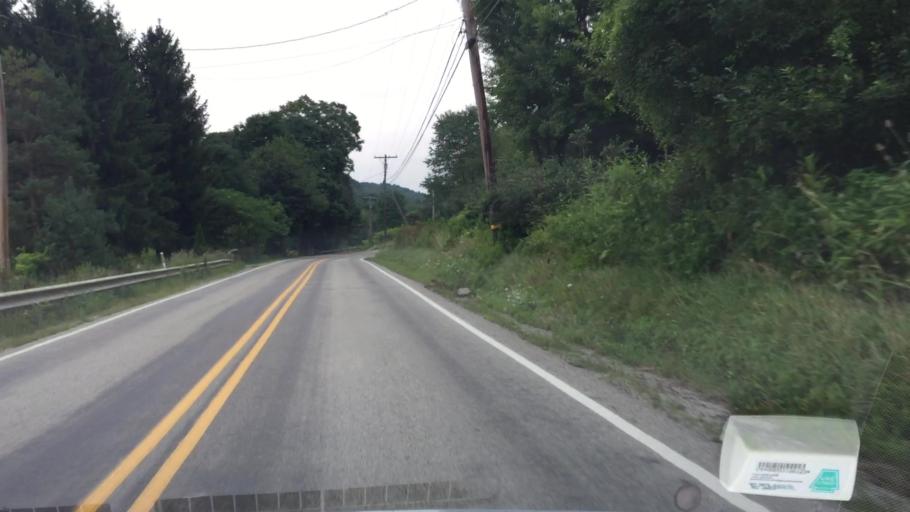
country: US
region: Pennsylvania
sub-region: Allegheny County
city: Curtisville
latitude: 40.6872
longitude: -79.8335
